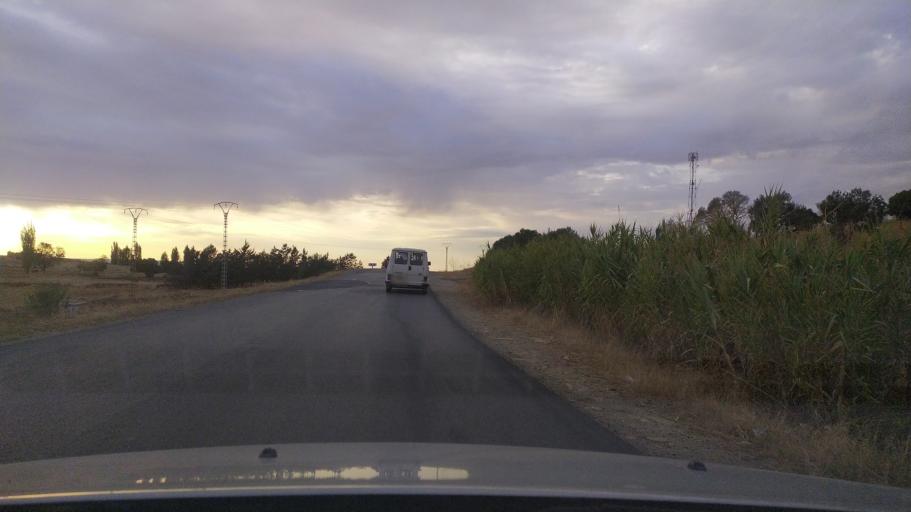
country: DZ
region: Tiaret
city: Frenda
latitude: 35.0209
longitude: 1.1029
